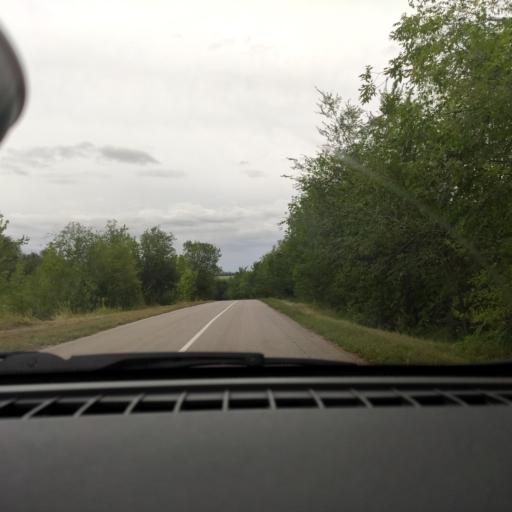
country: RU
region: Samara
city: Georgiyevka
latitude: 53.5126
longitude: 50.9939
